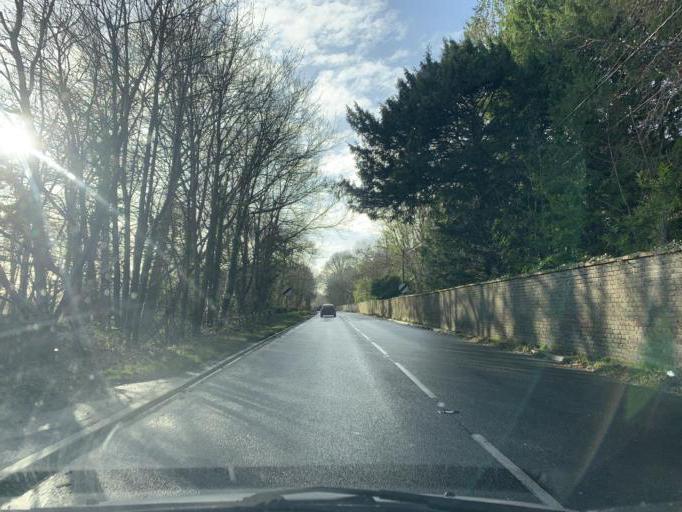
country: GB
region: England
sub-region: Wiltshire
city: Wilton
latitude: 51.0777
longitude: -1.8487
